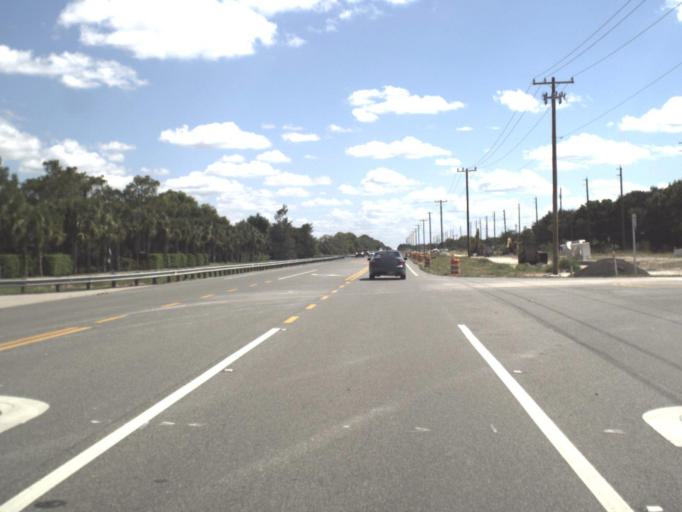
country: US
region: Florida
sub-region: Collier County
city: Lely Resort
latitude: 26.0414
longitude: -81.6649
